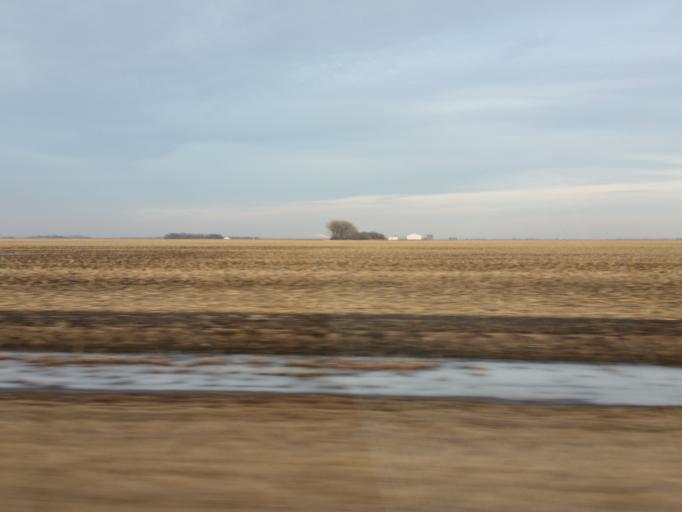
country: US
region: North Dakota
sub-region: Traill County
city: Mayville
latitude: 47.4189
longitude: -97.3261
